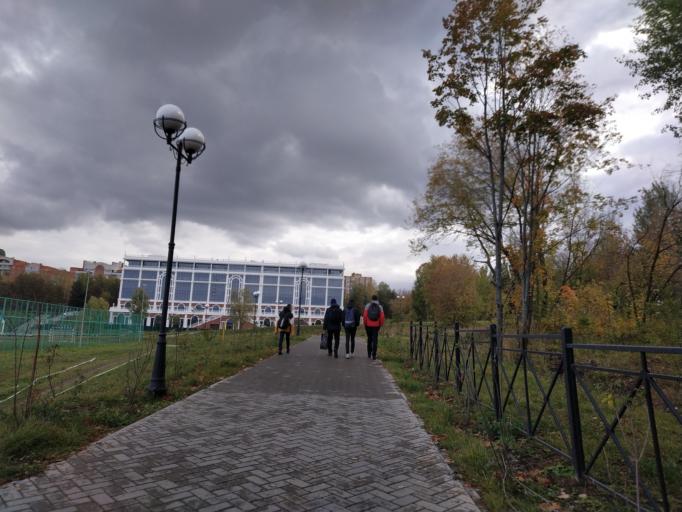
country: RU
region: Chuvashia
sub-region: Cheboksarskiy Rayon
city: Cheboksary
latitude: 56.1474
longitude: 47.2113
